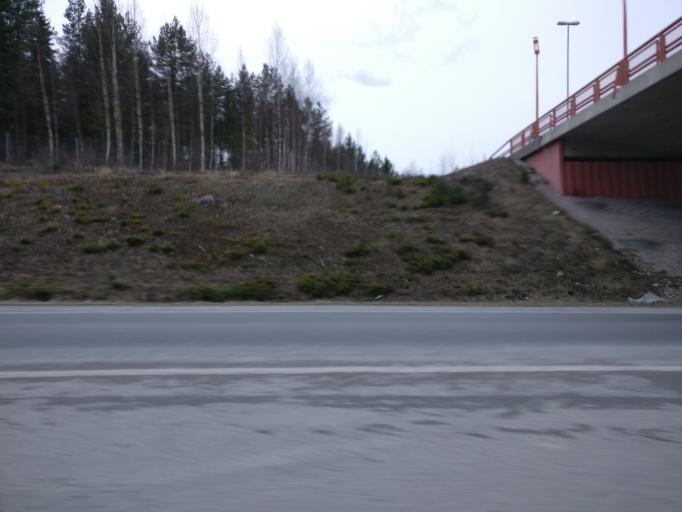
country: FI
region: Pirkanmaa
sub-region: Etelae-Pirkanmaa
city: Viiala
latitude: 61.2552
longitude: 23.8359
